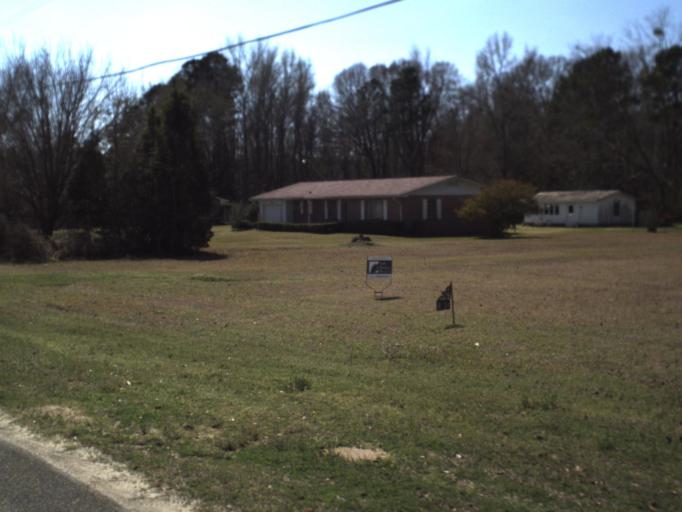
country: US
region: Florida
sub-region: Calhoun County
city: Blountstown
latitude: 30.4714
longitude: -85.0447
